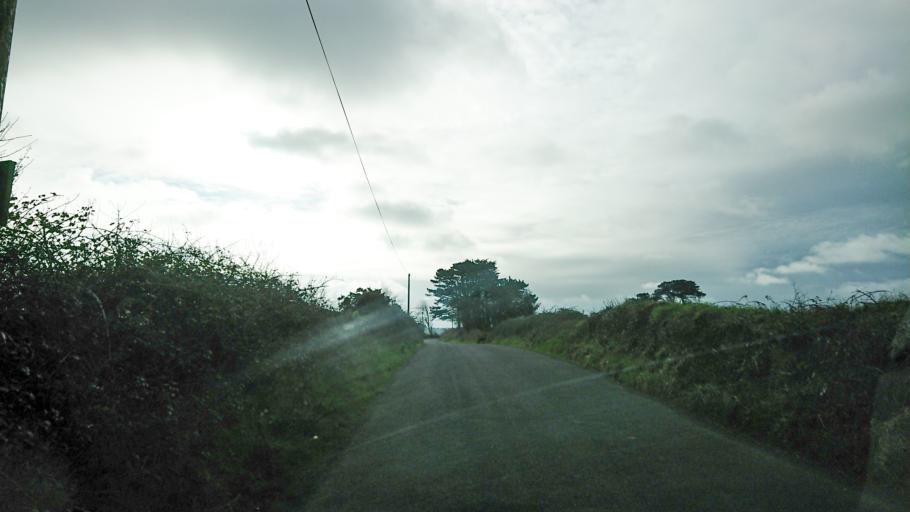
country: IE
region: Munster
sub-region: Waterford
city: Tra Mhor
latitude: 52.1735
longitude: -7.1764
